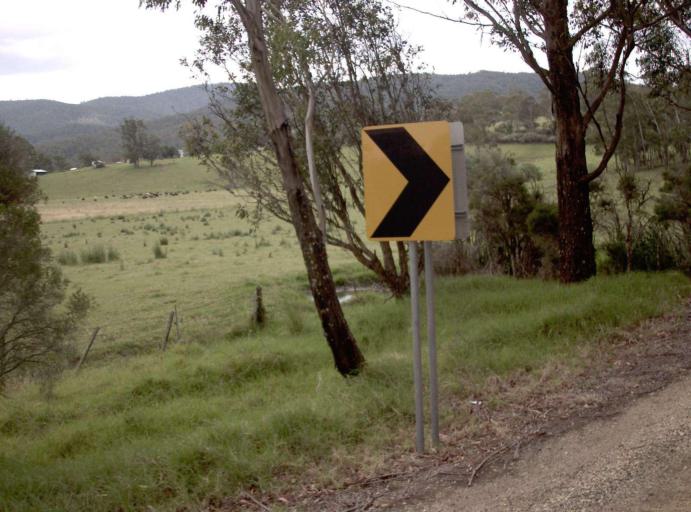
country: AU
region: New South Wales
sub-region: Bombala
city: Bombala
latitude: -37.4787
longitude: 149.1804
